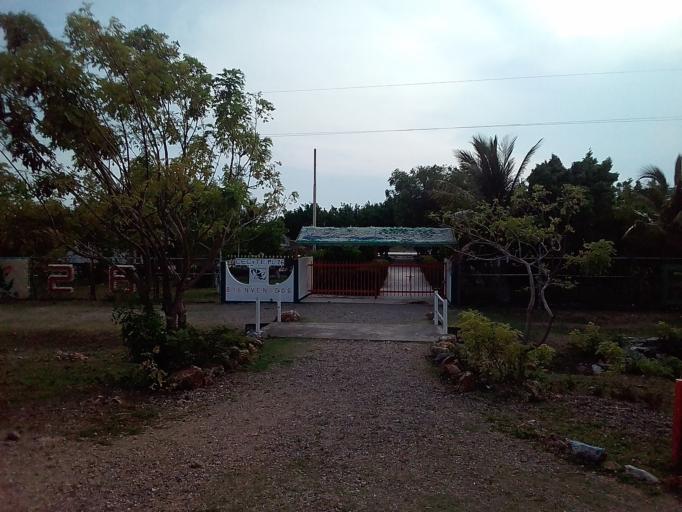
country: MX
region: Oaxaca
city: San Dionisio del Mar
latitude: 16.3361
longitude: -94.7581
